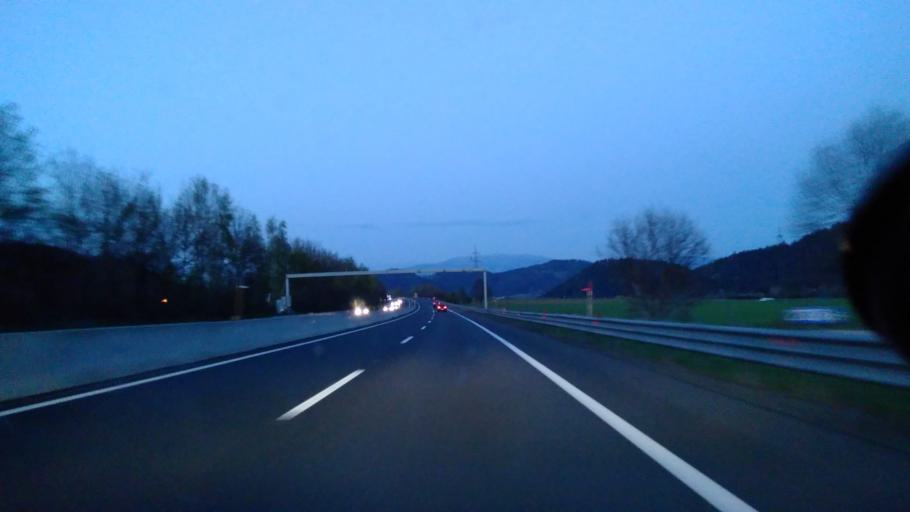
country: AT
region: Carinthia
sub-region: Politischer Bezirk Volkermarkt
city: Griffen
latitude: 46.6888
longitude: 14.7025
